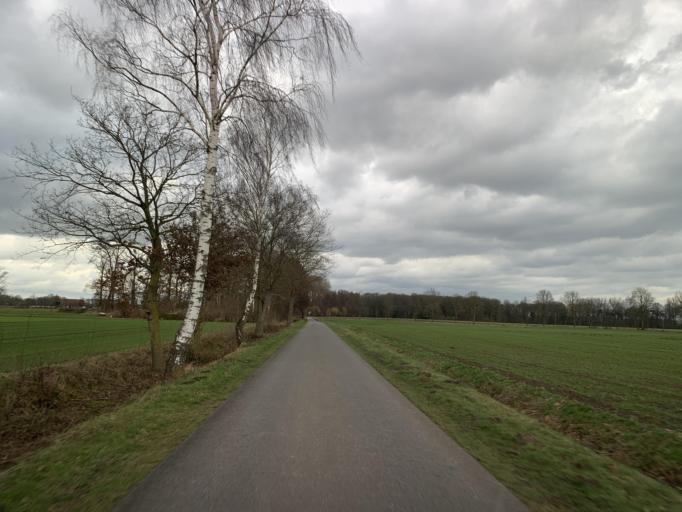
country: DE
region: North Rhine-Westphalia
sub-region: Regierungsbezirk Munster
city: Muenster
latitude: 52.0257
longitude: 7.6359
